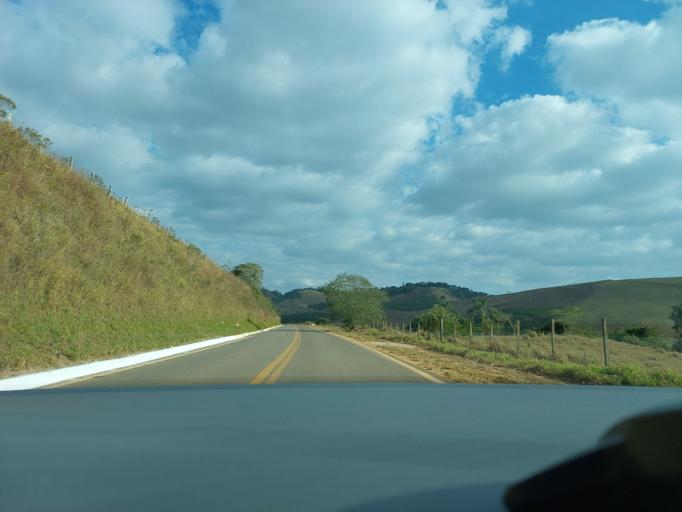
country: BR
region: Minas Gerais
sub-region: Visconde Do Rio Branco
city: Visconde do Rio Branco
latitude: -20.8634
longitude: -42.6708
